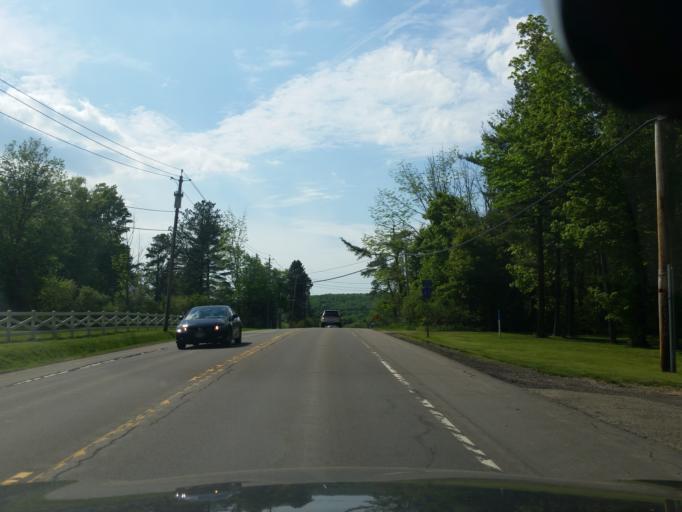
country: US
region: New York
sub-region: Chautauqua County
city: Lakewood
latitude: 42.1097
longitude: -79.3813
